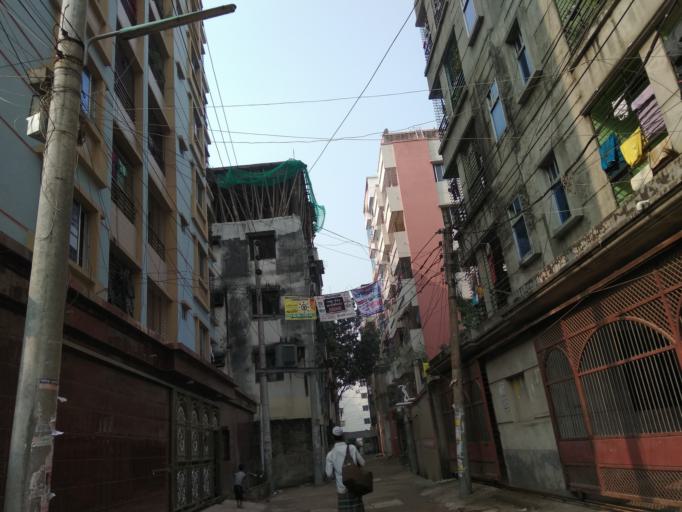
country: BD
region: Dhaka
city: Azimpur
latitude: 23.7673
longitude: 90.3541
